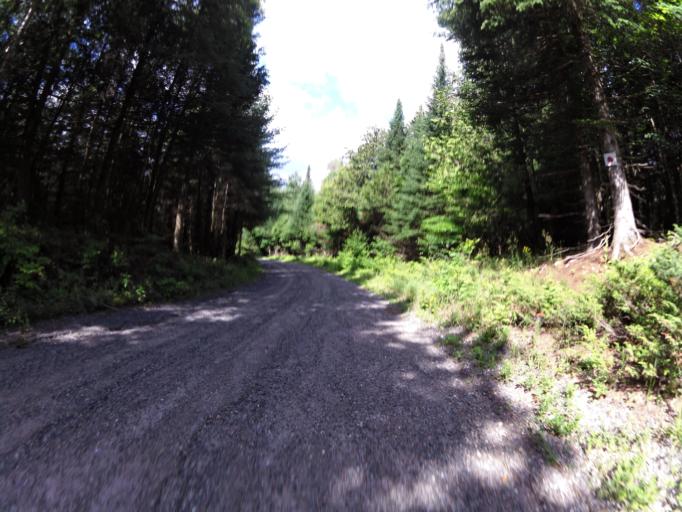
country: CA
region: Ontario
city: Perth
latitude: 45.0751
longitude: -76.4677
